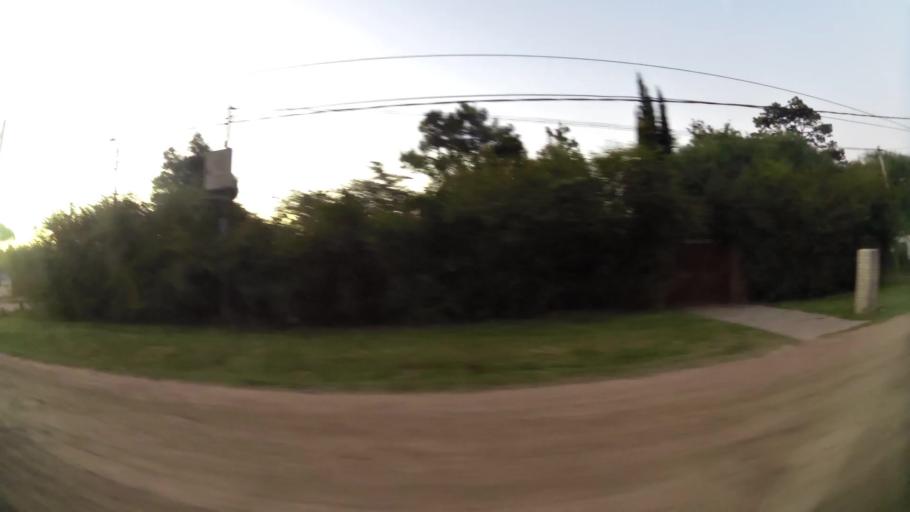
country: UY
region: Canelones
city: Colonia Nicolich
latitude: -34.8137
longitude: -55.9643
